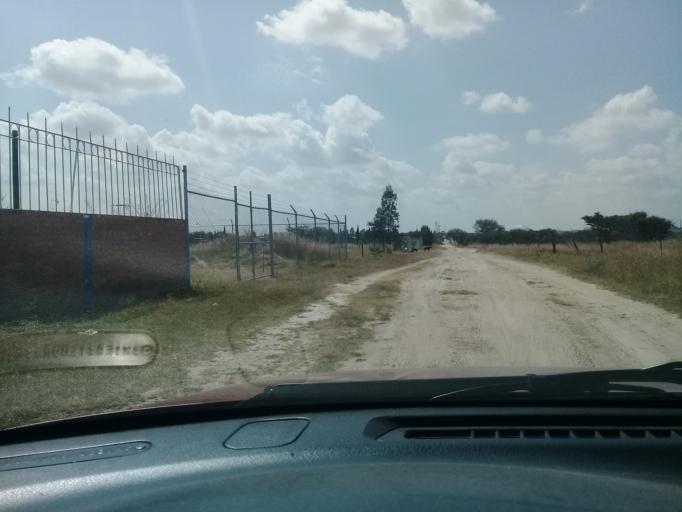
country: MX
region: Aguascalientes
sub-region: Aguascalientes
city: Penuelas (El Cienegal)
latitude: 21.7170
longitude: -102.3544
